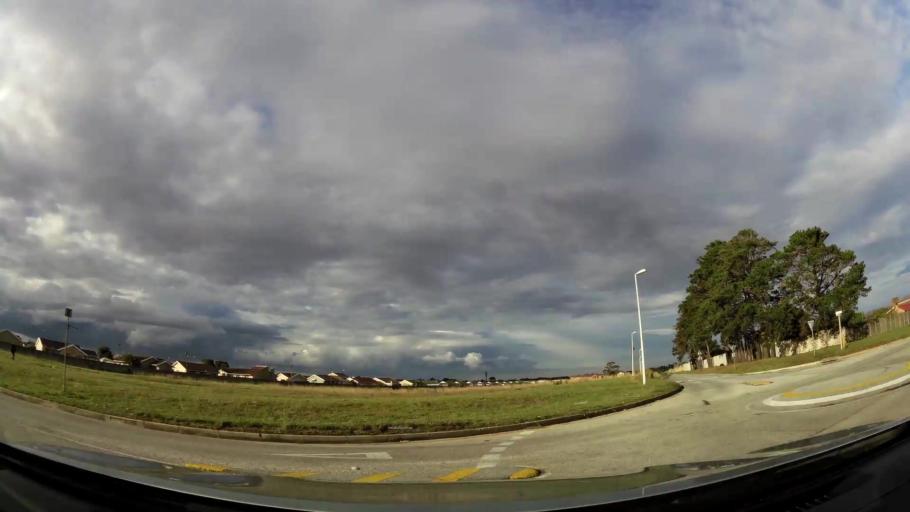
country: ZA
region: Eastern Cape
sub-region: Nelson Mandela Bay Metropolitan Municipality
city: Port Elizabeth
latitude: -33.9535
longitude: 25.4834
